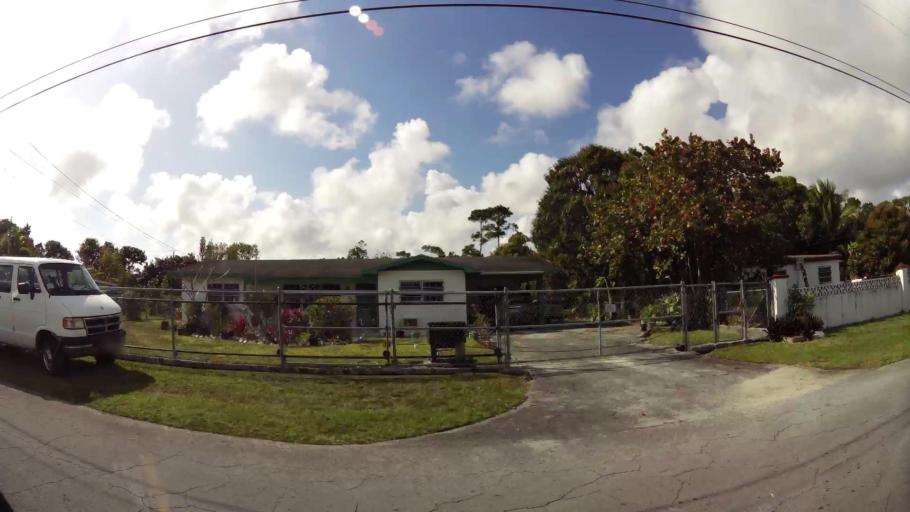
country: BS
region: Freeport
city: Freeport
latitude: 26.5228
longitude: -78.6856
